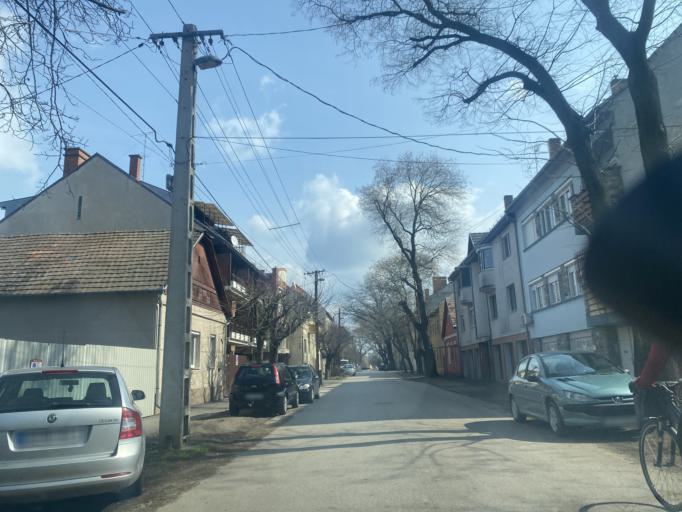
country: HU
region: Csongrad
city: Szeged
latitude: 46.2644
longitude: 20.1550
